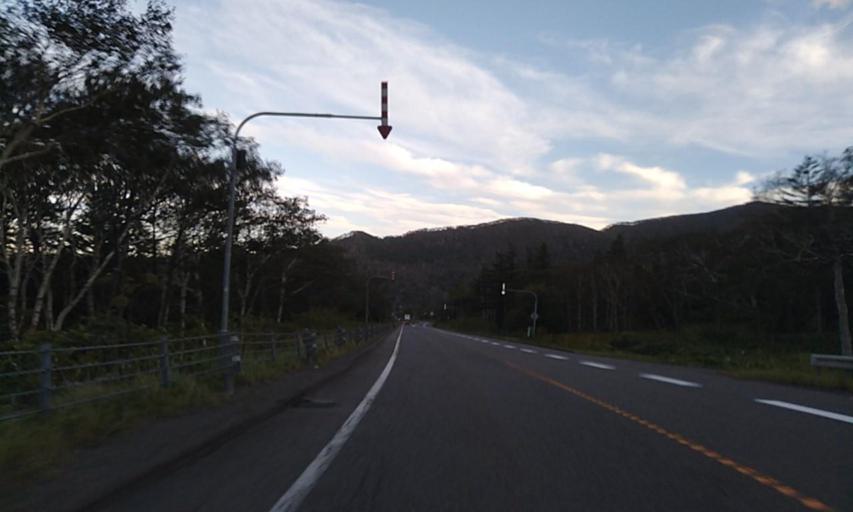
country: JP
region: Hokkaido
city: Otofuke
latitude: 42.9588
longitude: 142.7887
